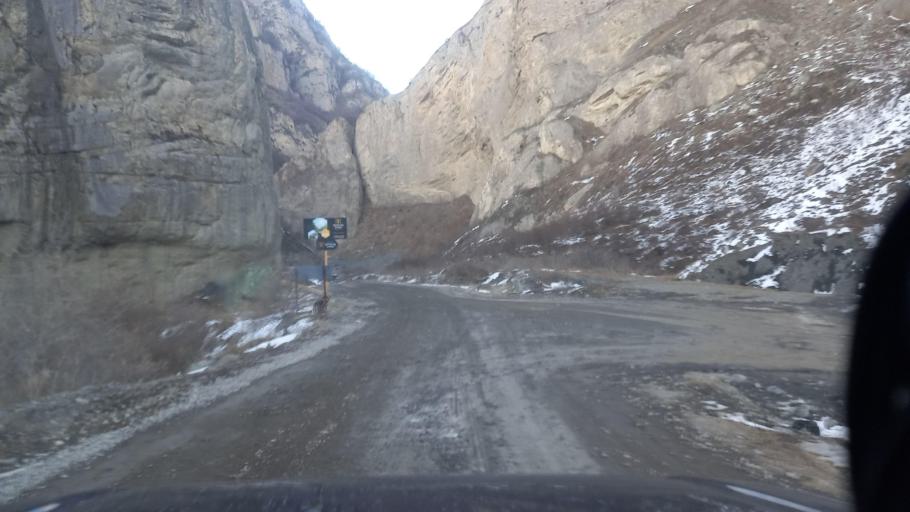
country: RU
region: Ingushetiya
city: Dzhayrakh
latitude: 42.8634
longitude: 44.5195
